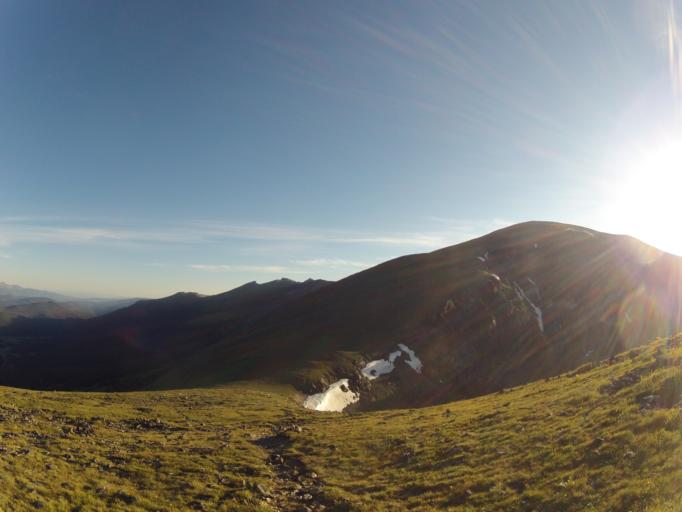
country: US
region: Colorado
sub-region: Larimer County
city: Estes Park
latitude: 40.4360
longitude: -105.7023
